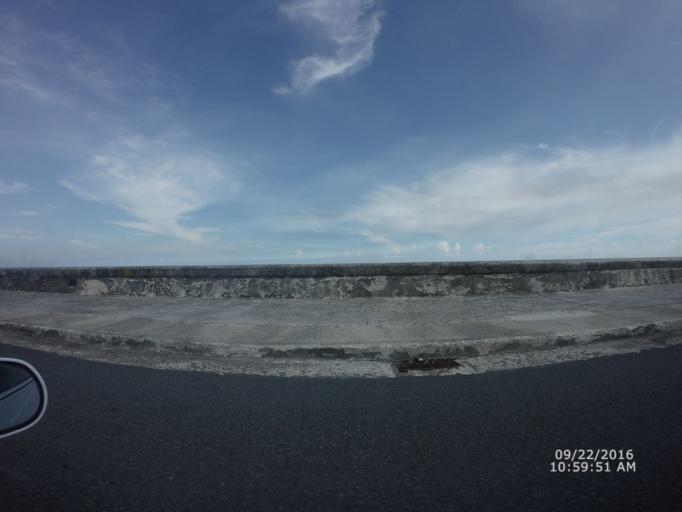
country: CU
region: La Habana
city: Havana
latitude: 23.1461
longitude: -82.3932
